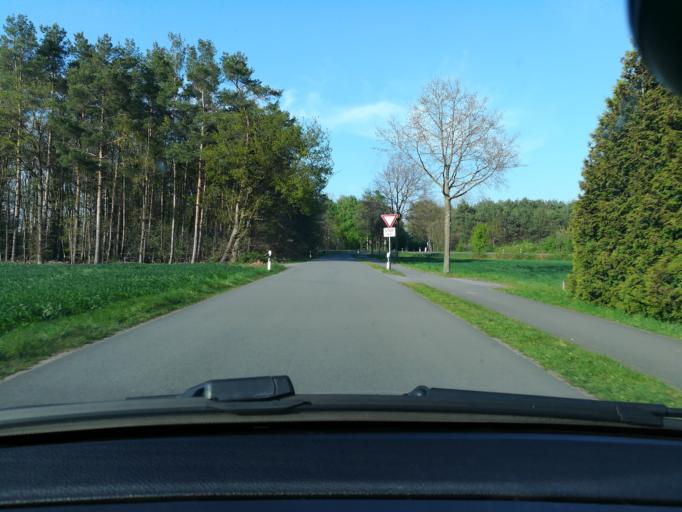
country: DE
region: North Rhine-Westphalia
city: Versmold
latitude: 52.0203
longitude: 8.1333
